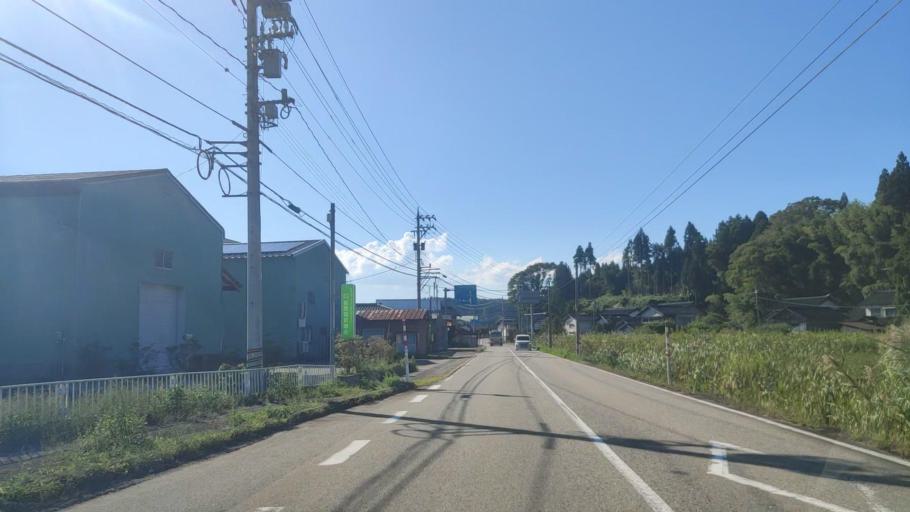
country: JP
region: Ishikawa
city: Nanao
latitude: 37.2348
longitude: 136.9682
